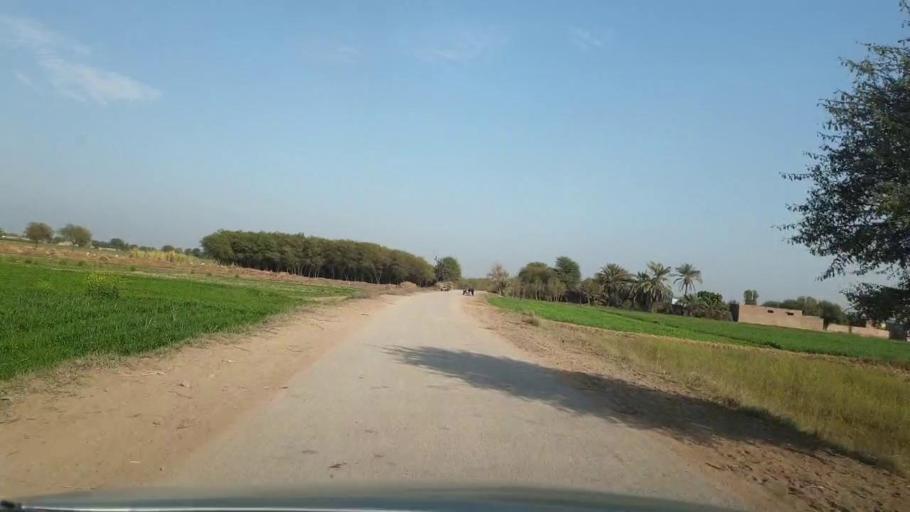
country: PK
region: Sindh
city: Tando Allahyar
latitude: 25.5937
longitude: 68.6725
